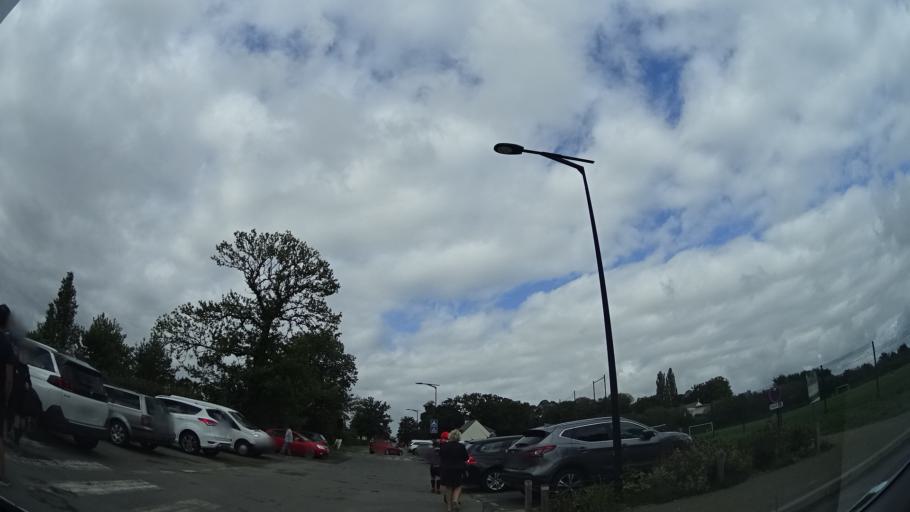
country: FR
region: Brittany
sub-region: Departement d'Ille-et-Vilaine
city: Saint-Medard-sur-Ille
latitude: 48.2653
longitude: -1.6089
